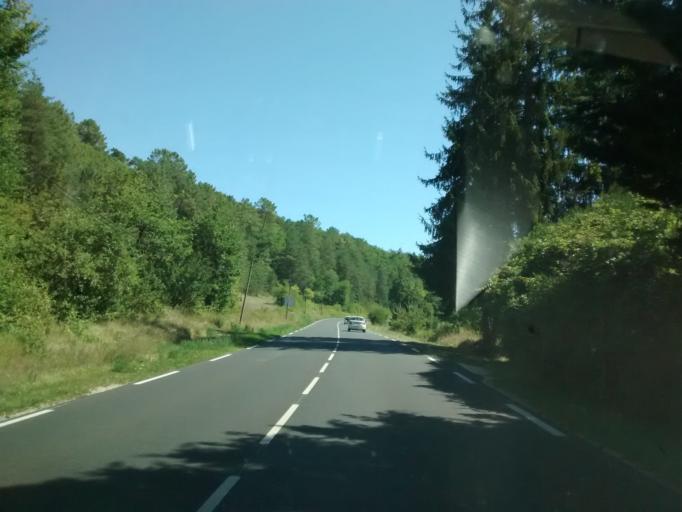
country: FR
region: Aquitaine
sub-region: Departement de la Dordogne
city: Boulazac
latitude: 45.1102
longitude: 0.8332
